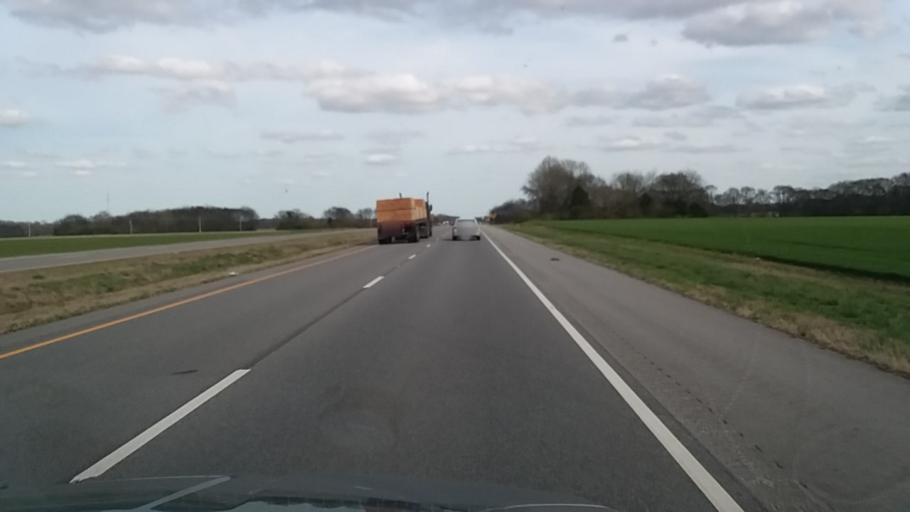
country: US
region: Alabama
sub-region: Lawrence County
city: Town Creek
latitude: 34.6839
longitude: -87.5349
